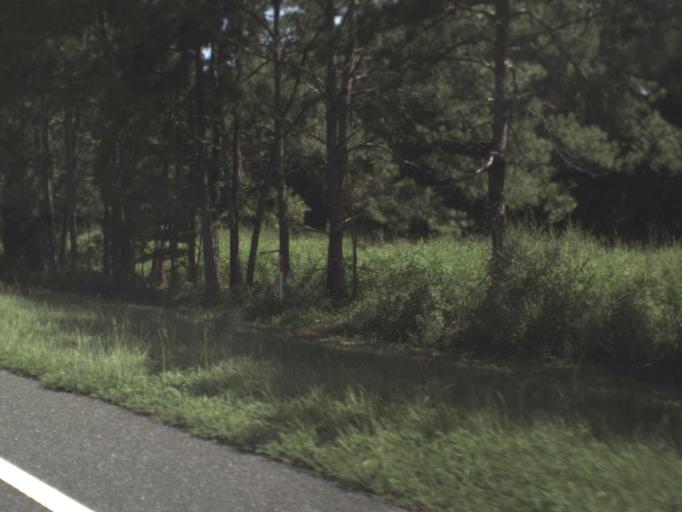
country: US
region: Florida
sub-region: Levy County
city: Chiefland
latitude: 29.4433
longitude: -82.8394
